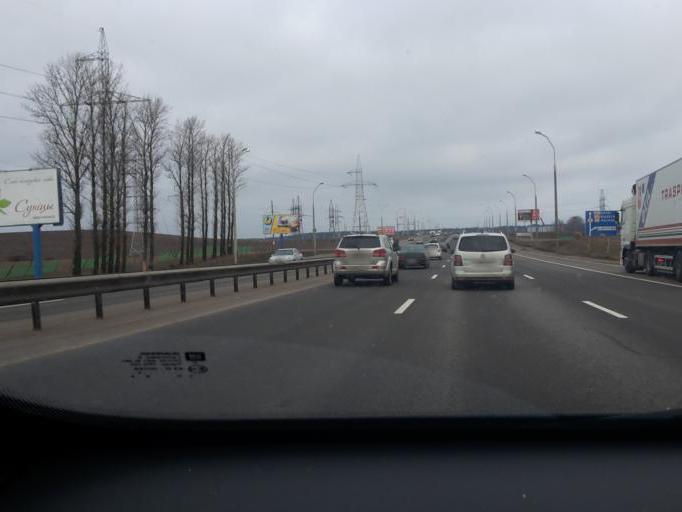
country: BY
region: Minsk
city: Novoye Medvezhino
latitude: 53.8896
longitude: 27.4130
